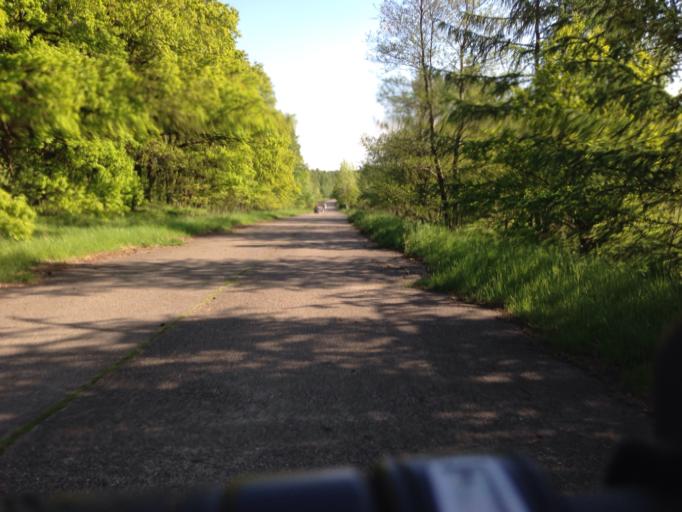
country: DE
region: Schleswig-Holstein
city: Stapelfeld
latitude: 53.6261
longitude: 10.2079
